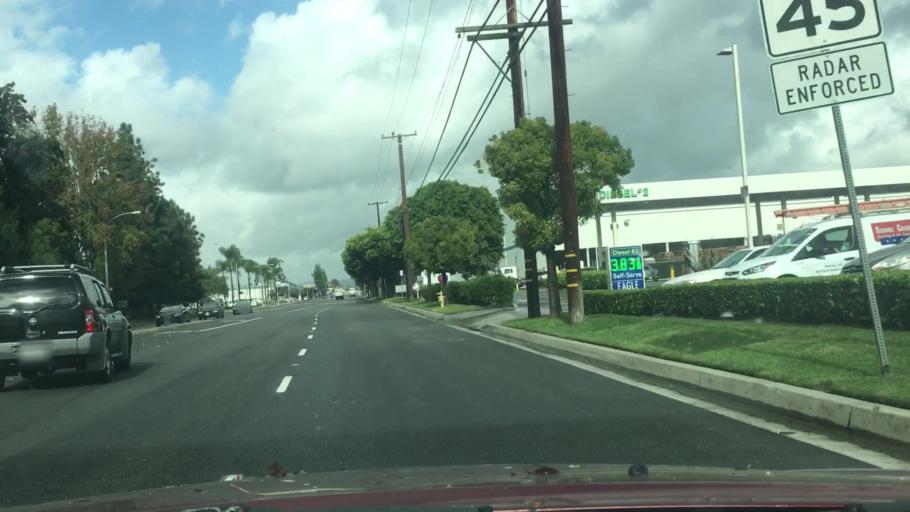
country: US
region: California
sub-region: Los Angeles County
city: La Mirada
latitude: 33.8887
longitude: -118.0289
